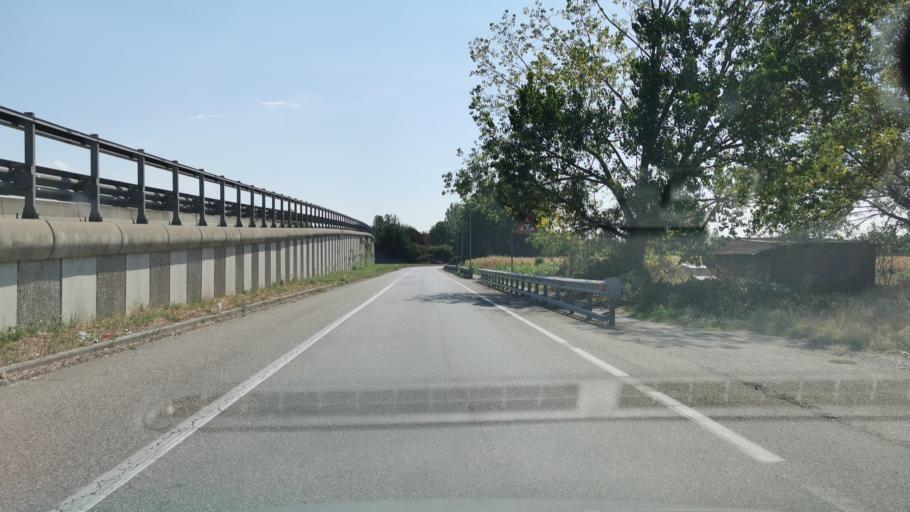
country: IT
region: Piedmont
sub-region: Provincia di Torino
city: Grugliasco
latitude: 45.0547
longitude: 7.5647
